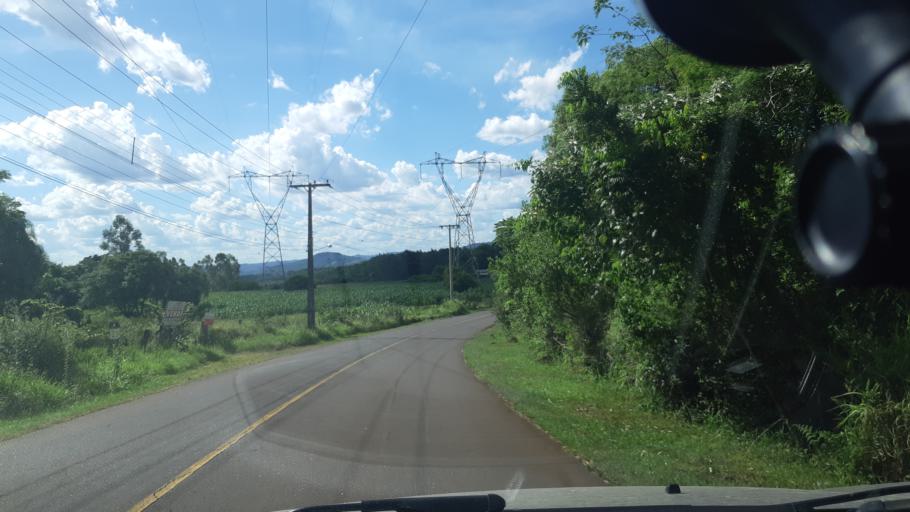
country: BR
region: Rio Grande do Sul
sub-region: Novo Hamburgo
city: Novo Hamburgo
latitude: -29.6261
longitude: -51.1084
